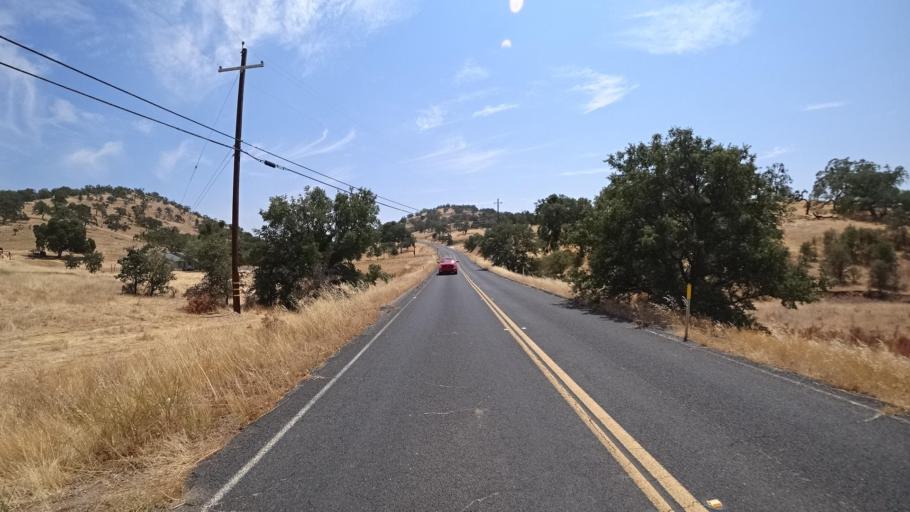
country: US
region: California
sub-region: Tuolumne County
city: Jamestown
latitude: 37.6716
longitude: -120.3575
